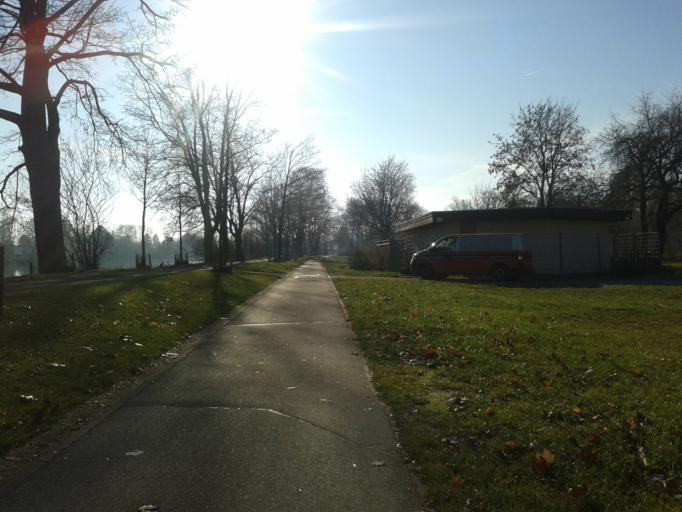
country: DE
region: Bavaria
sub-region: Swabia
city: Neu-Ulm
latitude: 48.4107
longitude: 10.0161
